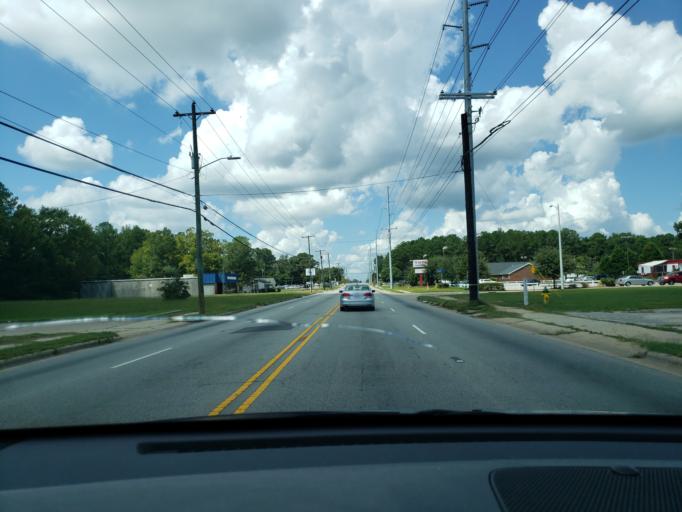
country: US
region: North Carolina
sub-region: Cumberland County
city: Fayetteville
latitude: 35.0913
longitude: -78.9107
